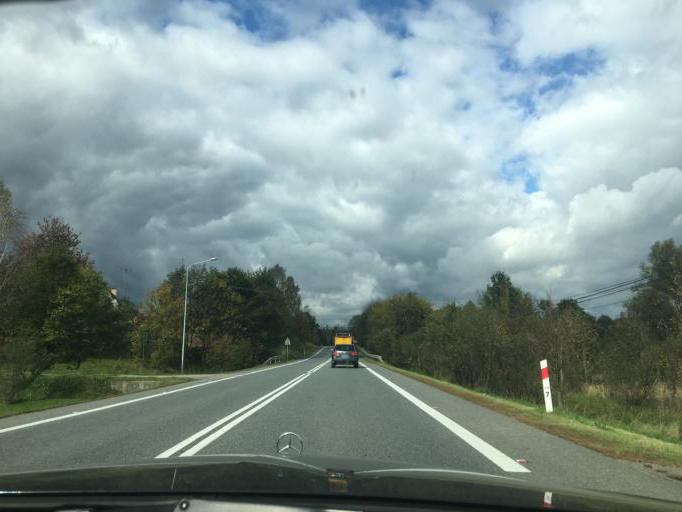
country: PL
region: Subcarpathian Voivodeship
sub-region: Powiat strzyzowski
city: Polomia
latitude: 49.8857
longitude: 21.8992
